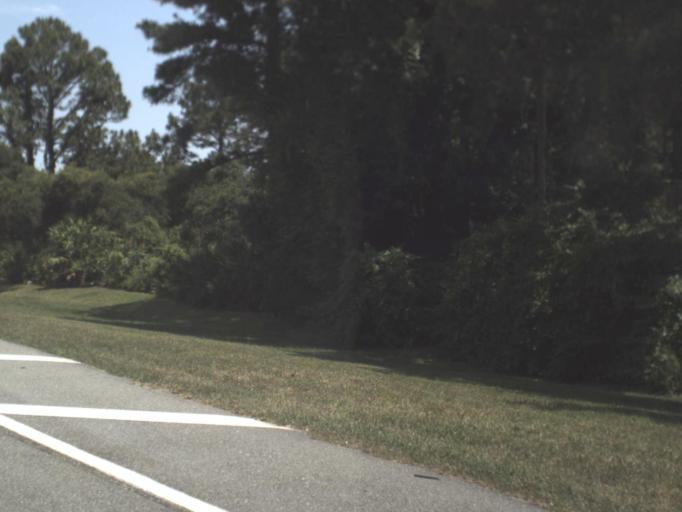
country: US
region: Florida
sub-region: Saint Johns County
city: Sawgrass
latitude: 30.2014
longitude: -81.3800
